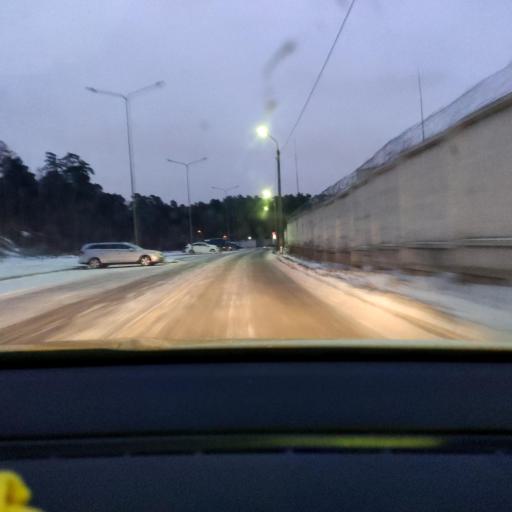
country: RU
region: Moscow
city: Rublevo
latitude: 55.7716
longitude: 37.3832
